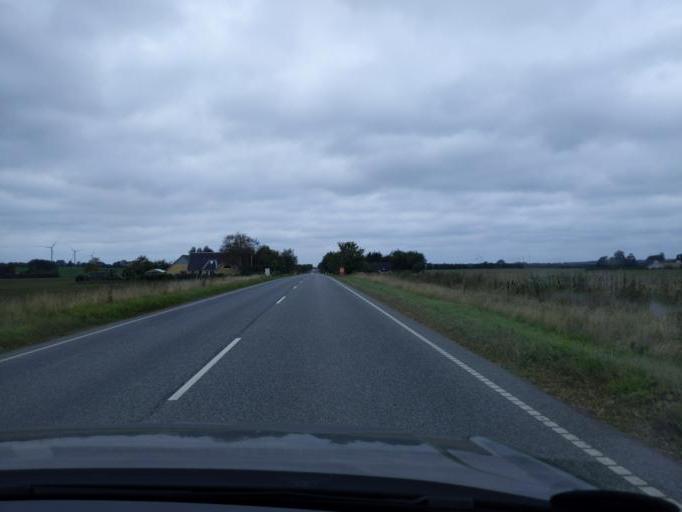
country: DK
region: Central Jutland
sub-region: Randers Kommune
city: Spentrup
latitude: 56.5288
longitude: 9.9202
